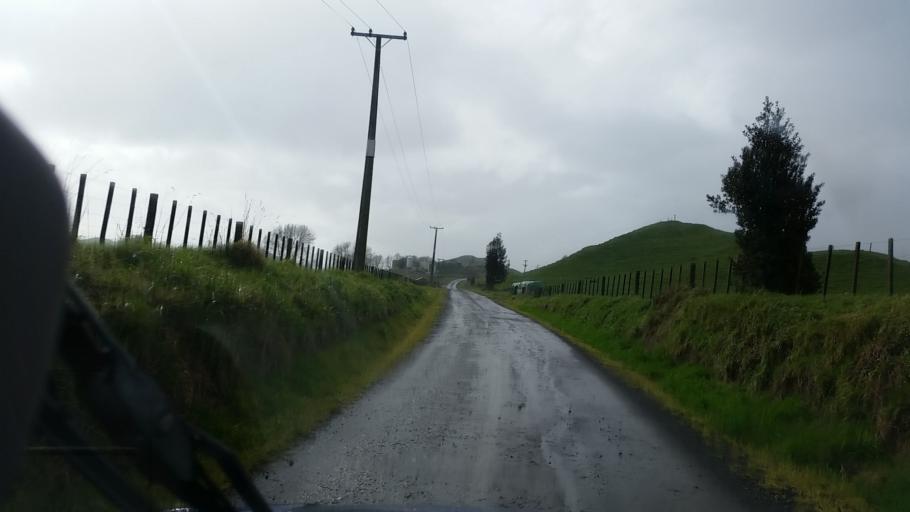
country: NZ
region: Taranaki
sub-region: South Taranaki District
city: Eltham
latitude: -39.3543
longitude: 174.4351
